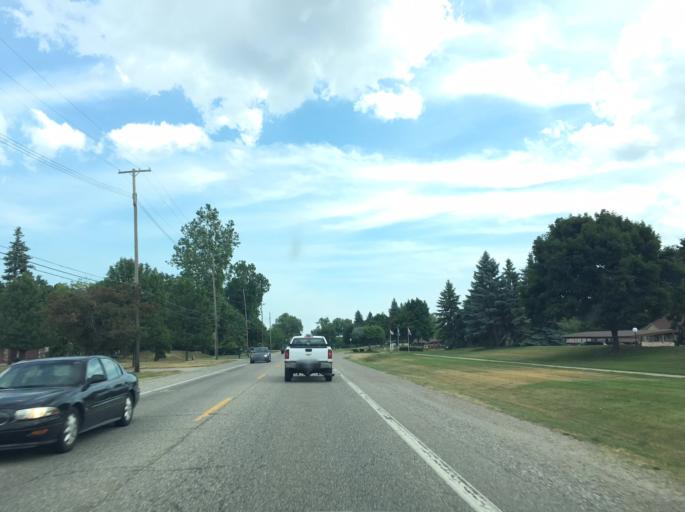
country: US
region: Michigan
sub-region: Macomb County
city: Utica
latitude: 42.6052
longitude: -83.0259
